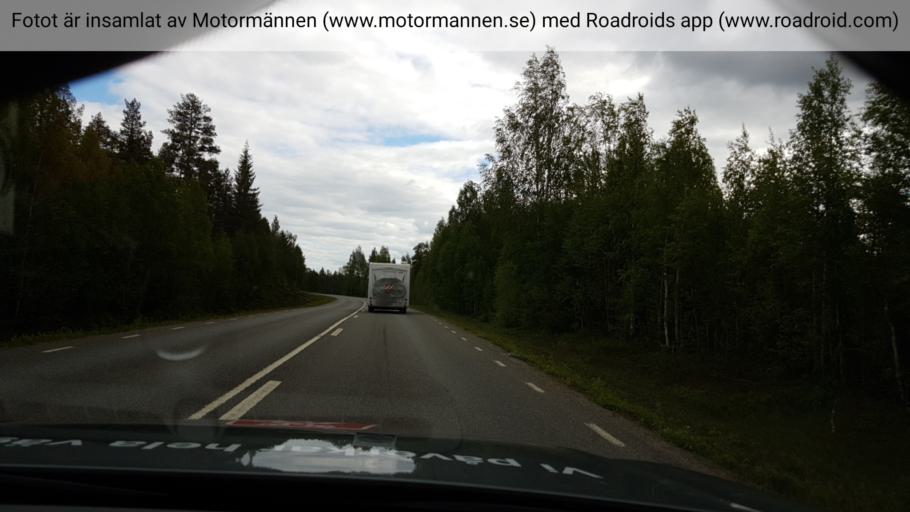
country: SE
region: Jaemtland
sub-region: Stroemsunds Kommun
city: Stroemsund
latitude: 64.3314
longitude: 15.1679
